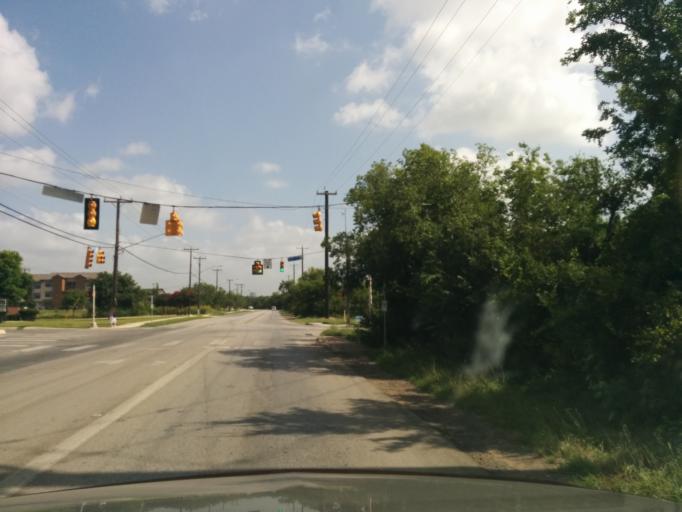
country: US
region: Texas
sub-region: Bexar County
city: Helotes
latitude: 29.5767
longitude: -98.6318
